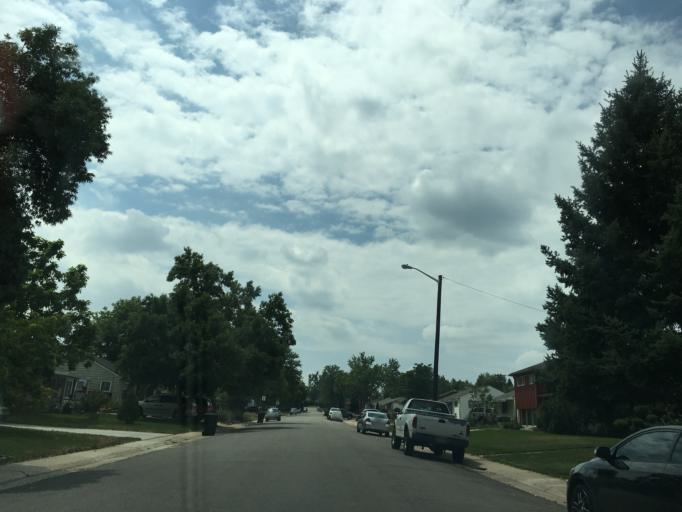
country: US
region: Colorado
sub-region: Arapahoe County
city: Sheridan
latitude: 39.6688
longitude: -105.0338
